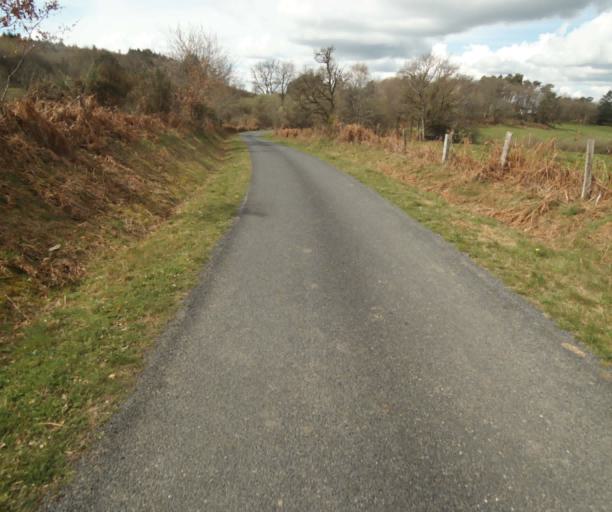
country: FR
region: Limousin
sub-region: Departement de la Correze
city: Correze
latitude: 45.3799
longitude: 1.9092
